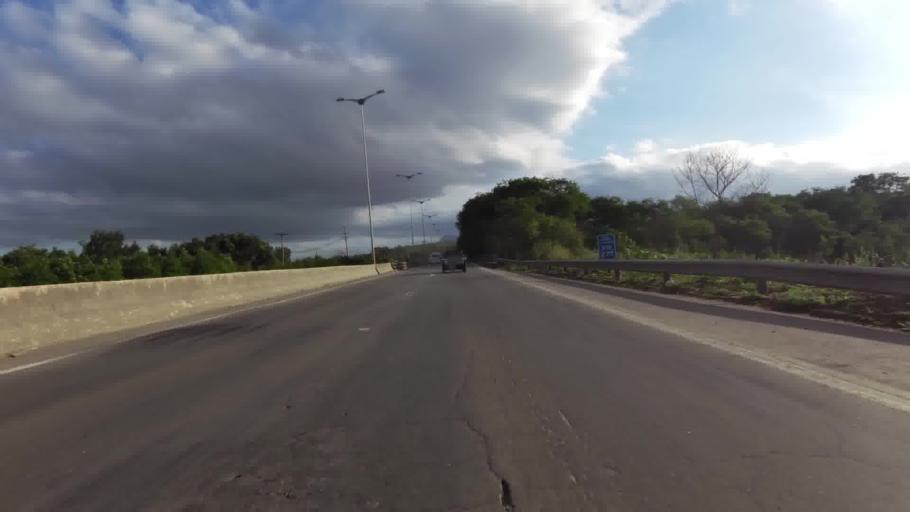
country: BR
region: Espirito Santo
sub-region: Serra
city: Serra
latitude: -20.2131
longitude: -40.3213
